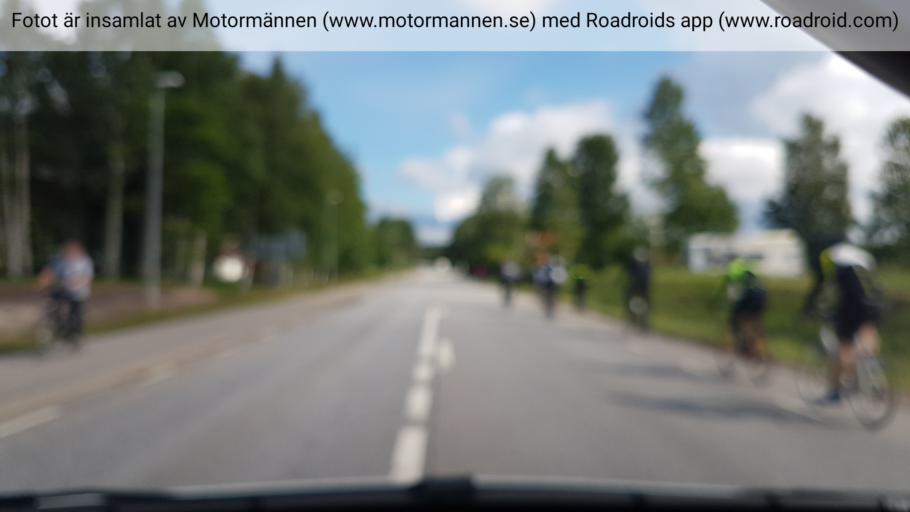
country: SE
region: Vaestra Goetaland
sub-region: Karlsborgs Kommun
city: Karlsborg
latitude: 58.5529
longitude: 14.5002
